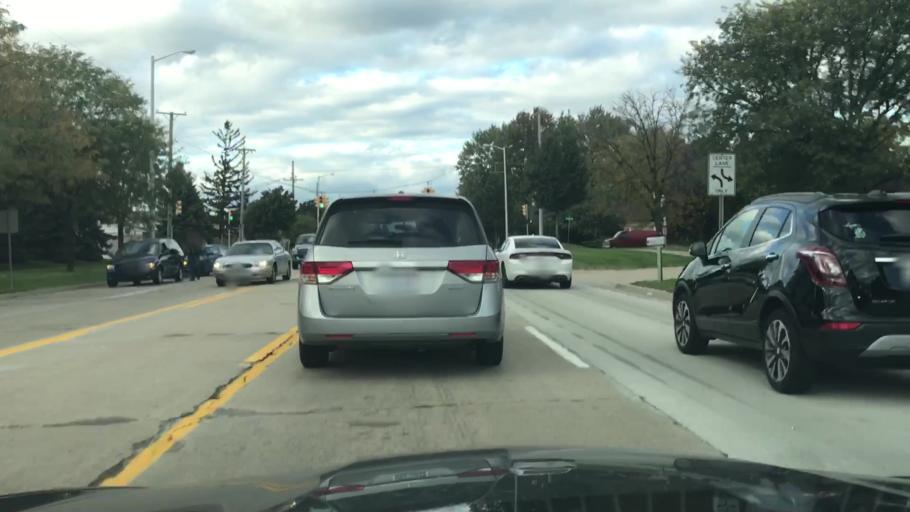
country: US
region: Michigan
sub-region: Macomb County
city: Sterling Heights
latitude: 42.5852
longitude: -83.0704
